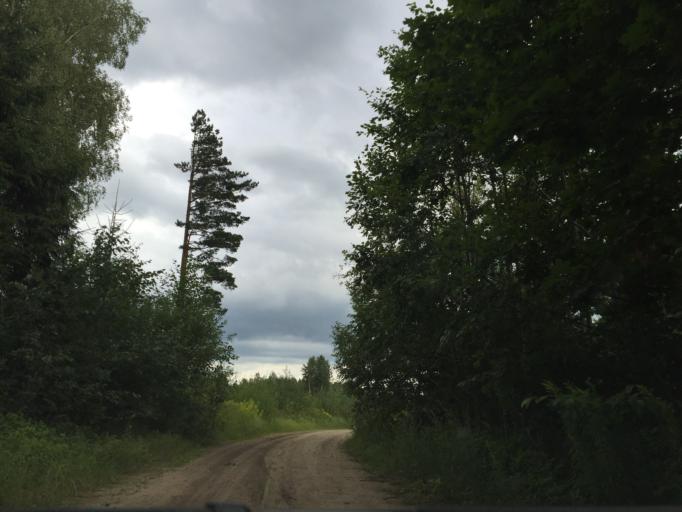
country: LV
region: Saulkrastu
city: Saulkrasti
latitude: 57.2356
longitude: 24.4632
